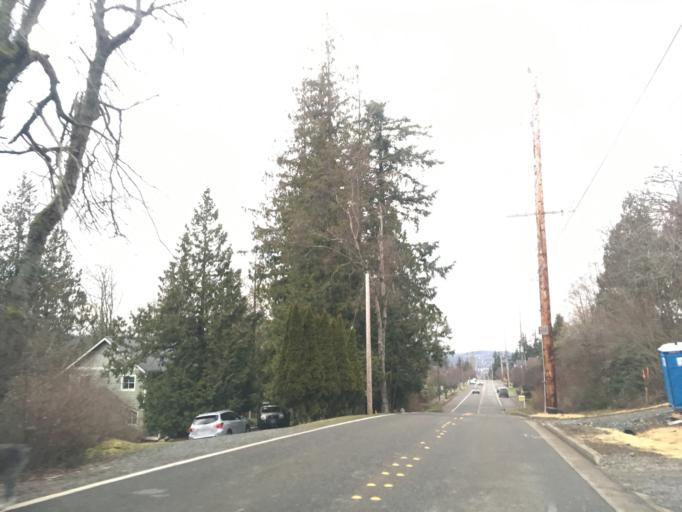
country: US
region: Washington
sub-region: Whatcom County
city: Bellingham
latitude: 48.7210
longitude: -122.4643
